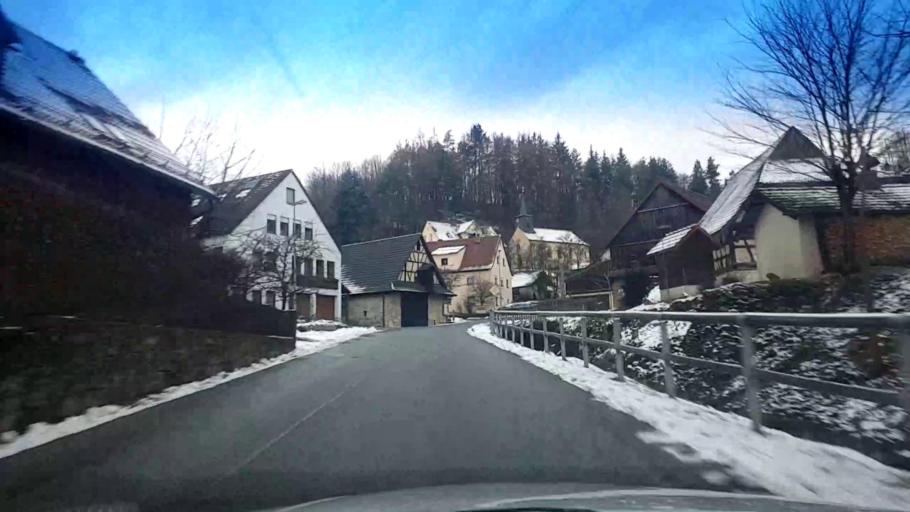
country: DE
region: Bavaria
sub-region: Upper Franconia
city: Buttenheim
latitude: 49.8500
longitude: 11.0784
